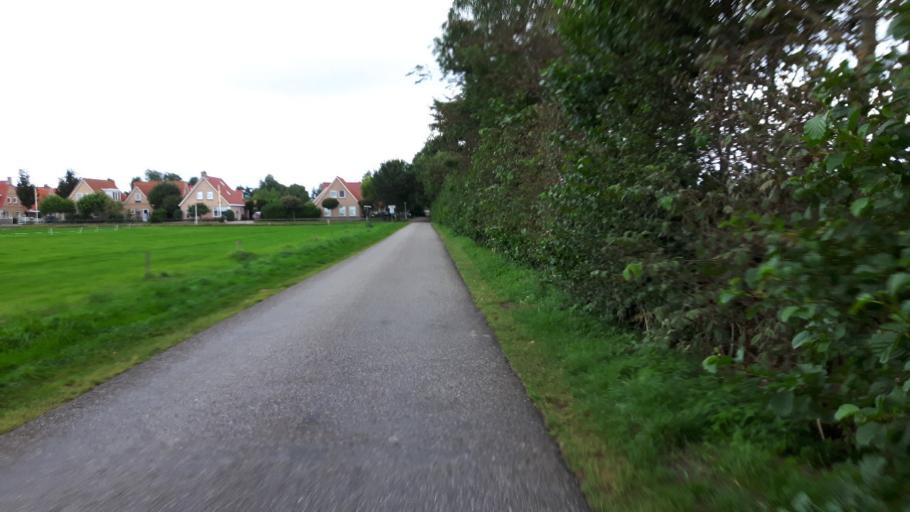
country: NL
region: Friesland
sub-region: Gemeente Ameland
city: Hollum
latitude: 53.4423
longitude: 5.6448
